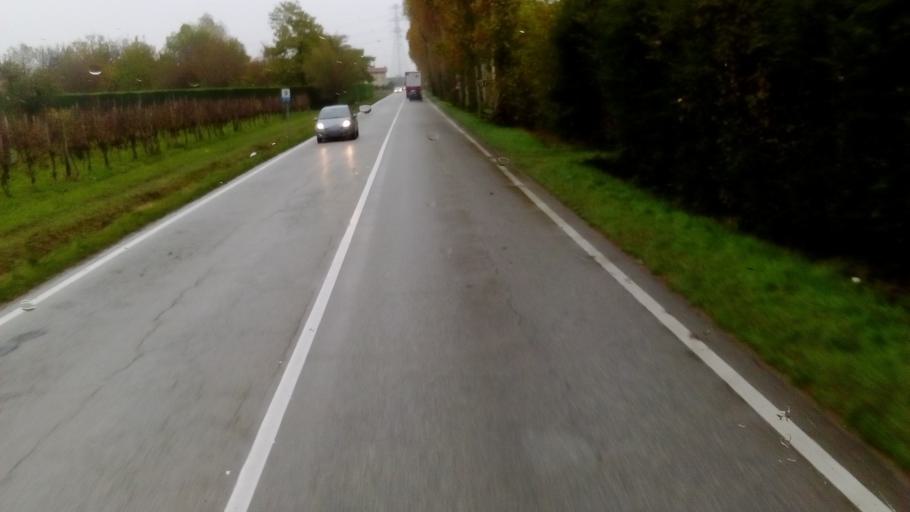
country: IT
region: Veneto
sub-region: Provincia di Vicenza
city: Montecchio Precalcino
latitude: 45.6789
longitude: 11.5702
